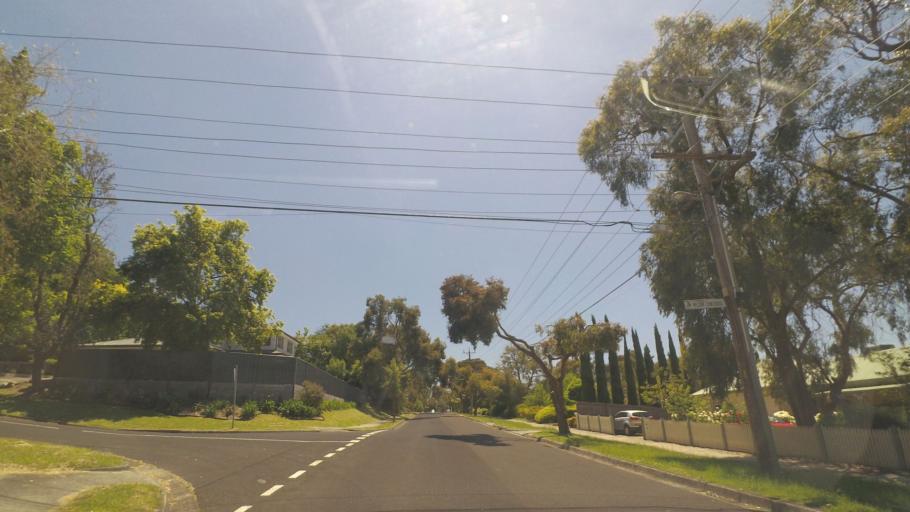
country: AU
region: Victoria
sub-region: Maroondah
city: Croydon North
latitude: -37.7727
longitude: 145.2868
